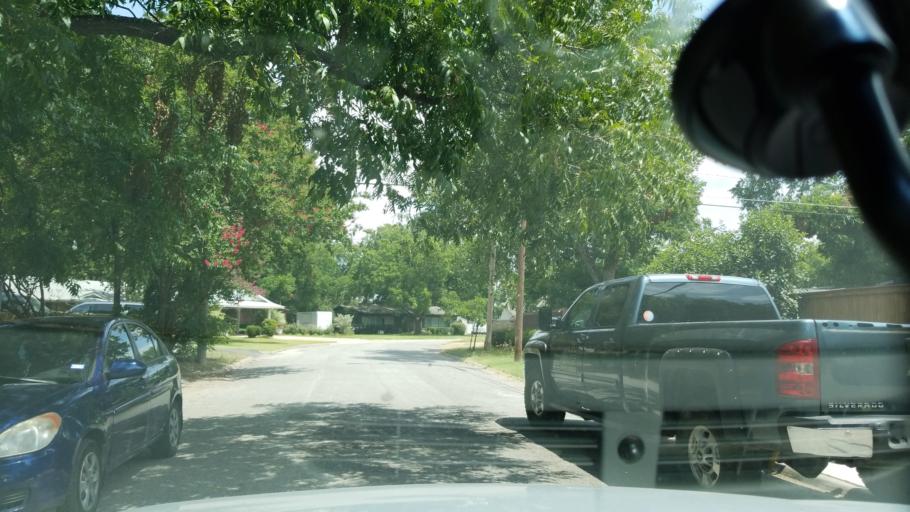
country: US
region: Texas
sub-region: Dallas County
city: Grand Prairie
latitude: 32.7545
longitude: -96.9891
